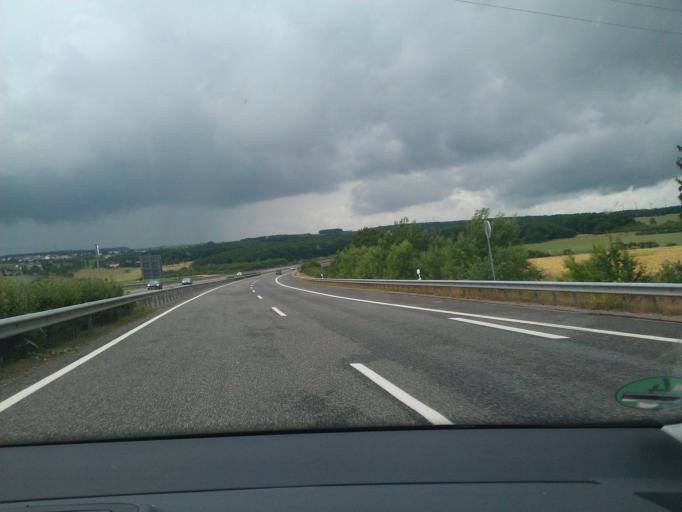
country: DE
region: Rheinland-Pfalz
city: Gransdorf
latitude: 50.0086
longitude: 6.6851
